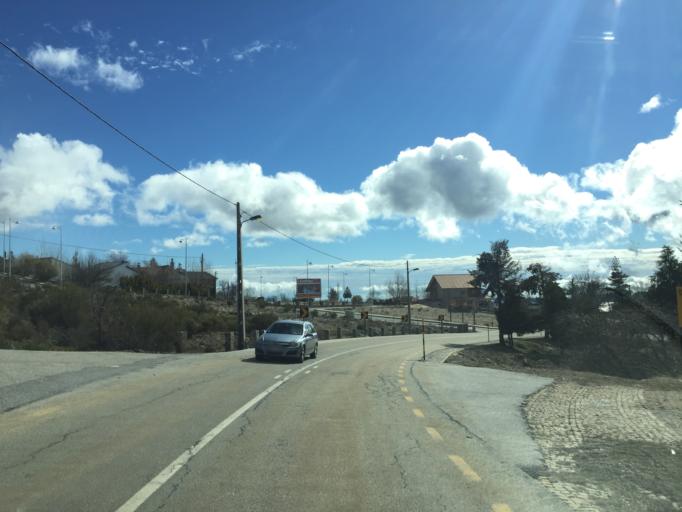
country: PT
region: Castelo Branco
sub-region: Covilha
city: Covilha
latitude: 40.3099
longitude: -7.5507
